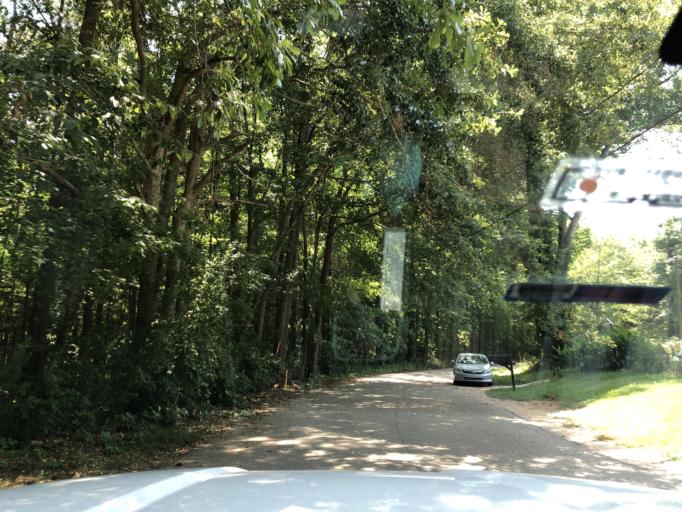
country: US
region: Georgia
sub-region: Fulton County
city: Fairburn
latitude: 33.5631
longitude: -84.5895
